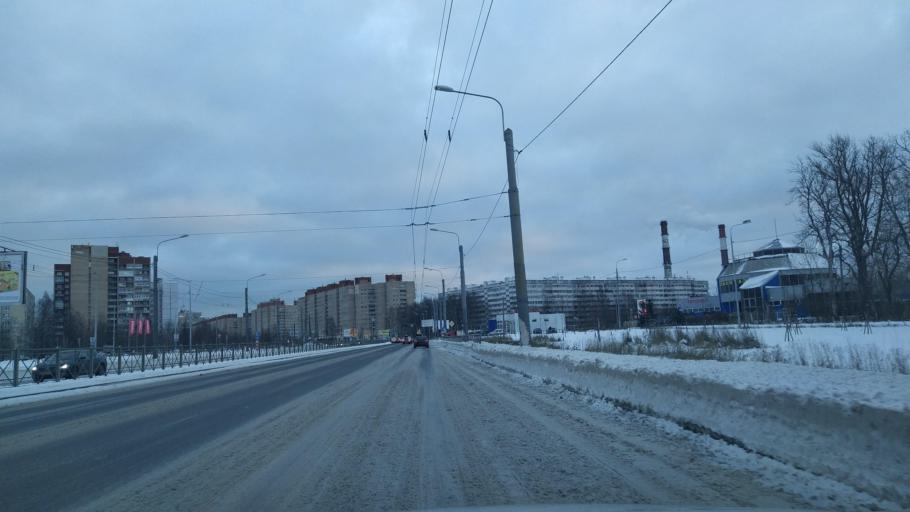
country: RU
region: St.-Petersburg
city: Komendantsky aerodrom
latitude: 59.9989
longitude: 30.2716
